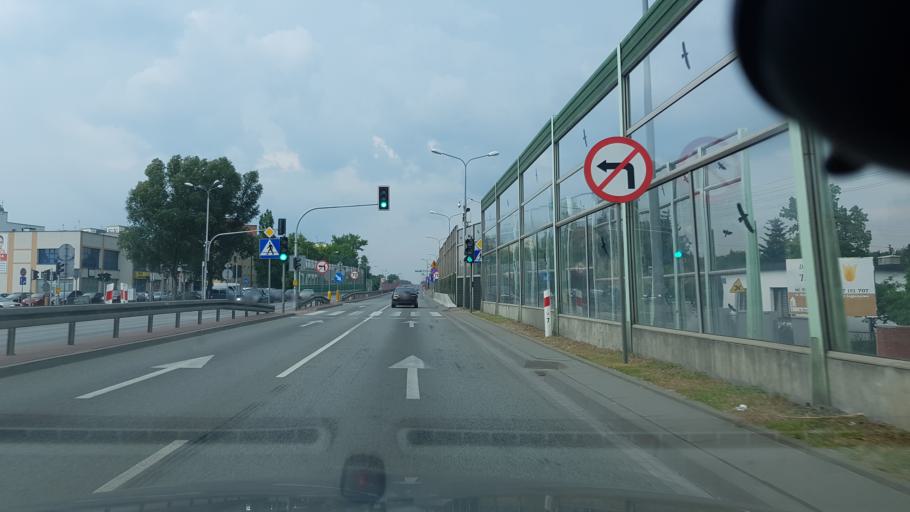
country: PL
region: Masovian Voivodeship
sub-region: Powiat legionowski
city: Legionowo
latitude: 52.3948
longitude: 20.9378
